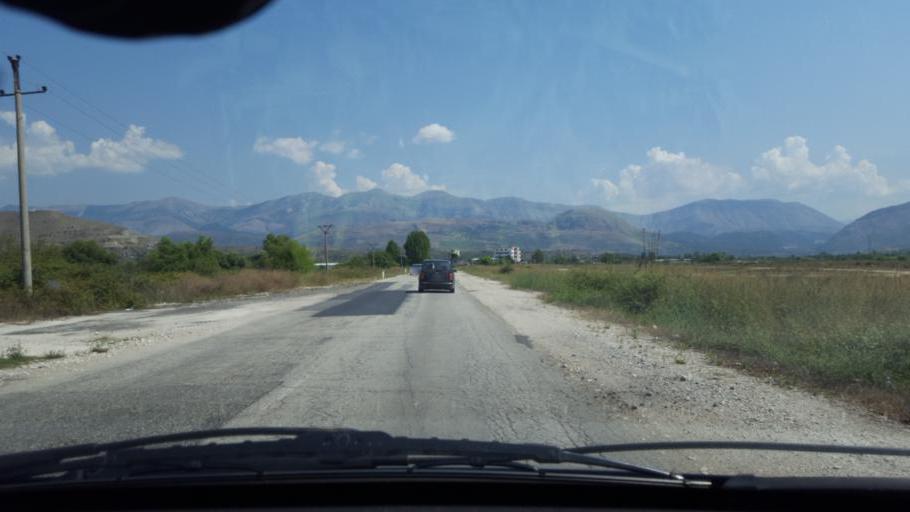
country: AL
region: Vlore
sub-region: Rrethi i Delvines
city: Finiq
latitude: 39.8862
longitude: 20.0586
